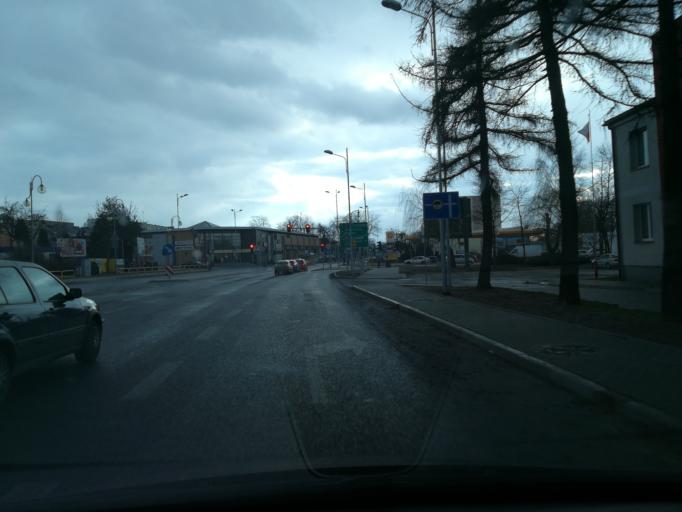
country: PL
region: Lodz Voivodeship
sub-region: Powiat radomszczanski
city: Radomsko
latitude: 51.0653
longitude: 19.4446
